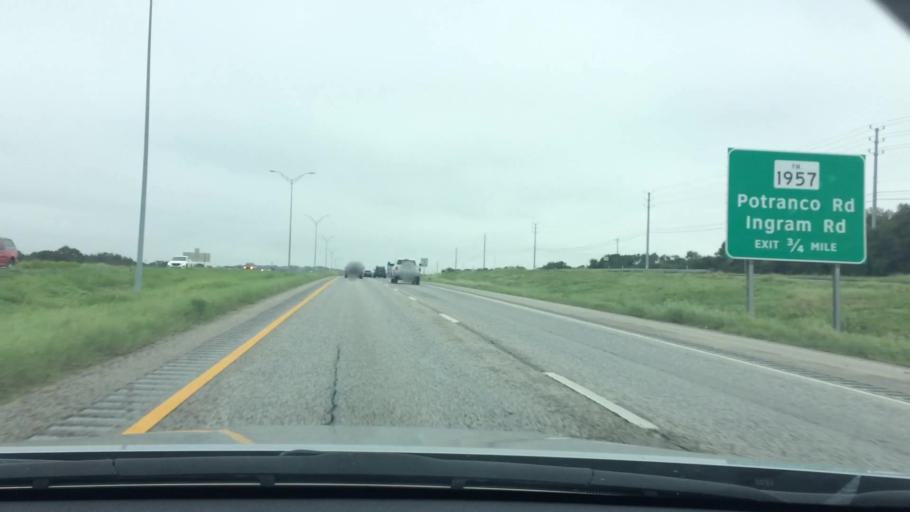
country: US
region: Texas
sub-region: Bexar County
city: Leon Valley
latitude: 29.4588
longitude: -98.6897
